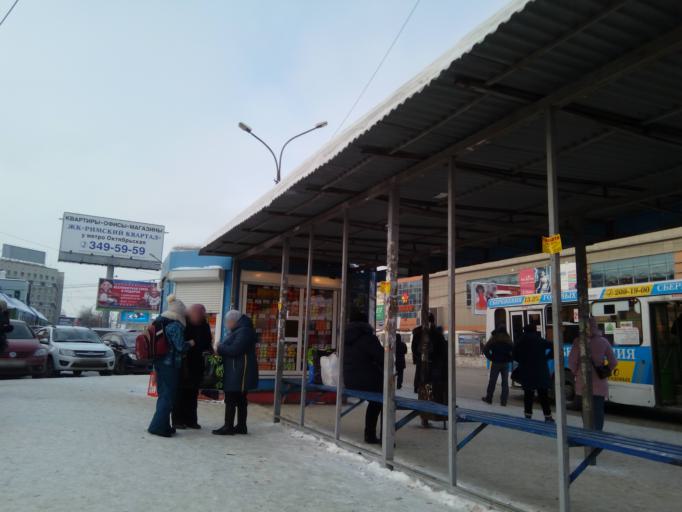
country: RU
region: Novosibirsk
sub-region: Novosibirskiy Rayon
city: Novosibirsk
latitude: 54.9829
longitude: 82.8929
